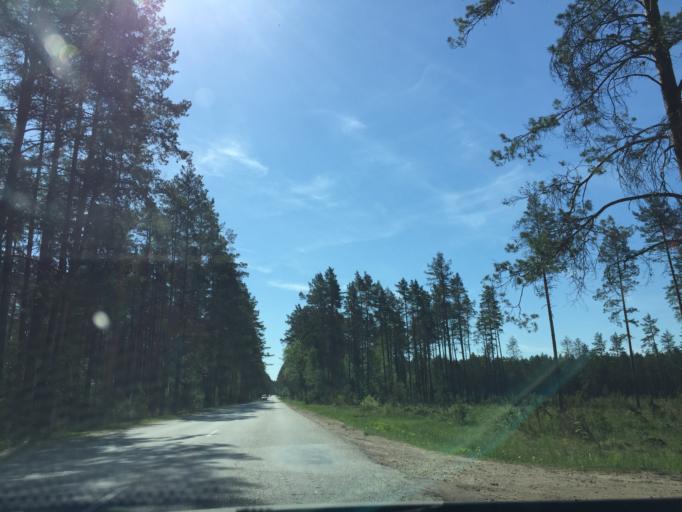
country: LV
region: Garkalne
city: Garkalne
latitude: 57.0325
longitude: 24.4227
